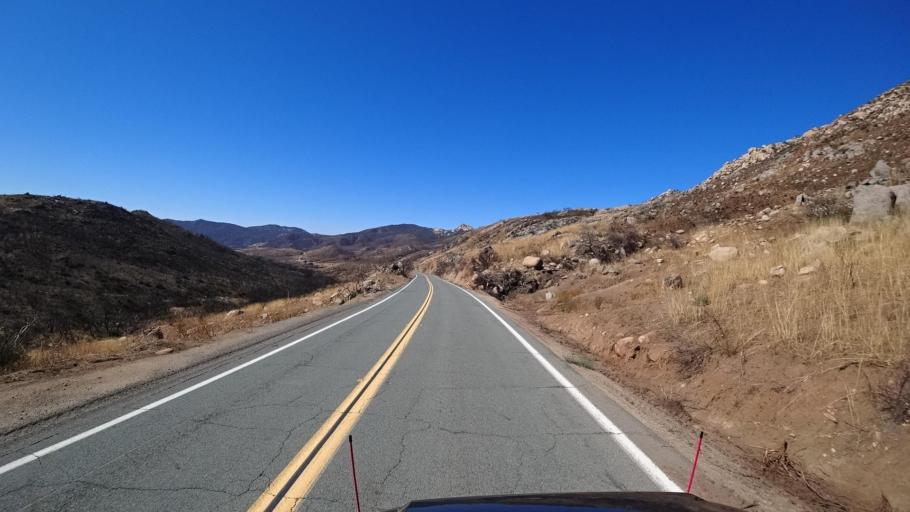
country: US
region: California
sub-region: San Diego County
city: Alpine
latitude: 32.7431
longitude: -116.6810
